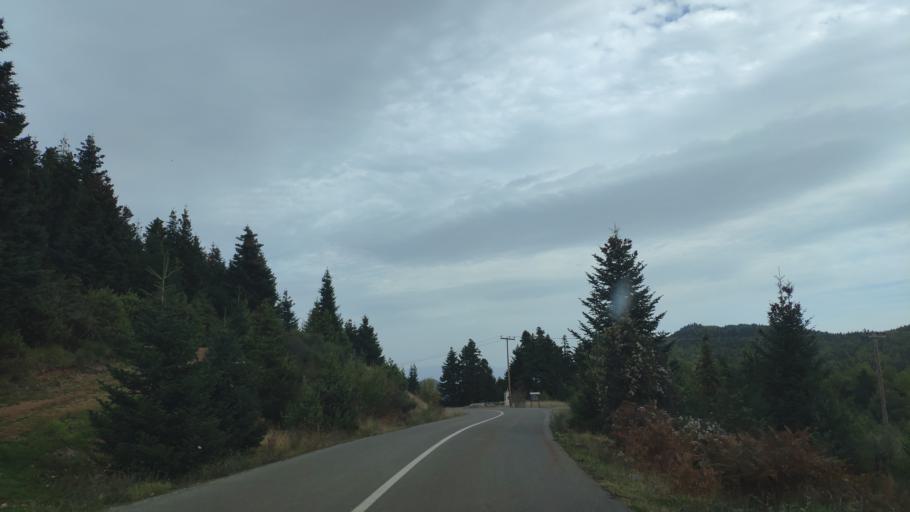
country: GR
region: Central Greece
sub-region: Nomos Fthiotidos
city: Stavros
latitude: 38.7107
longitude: 22.3235
